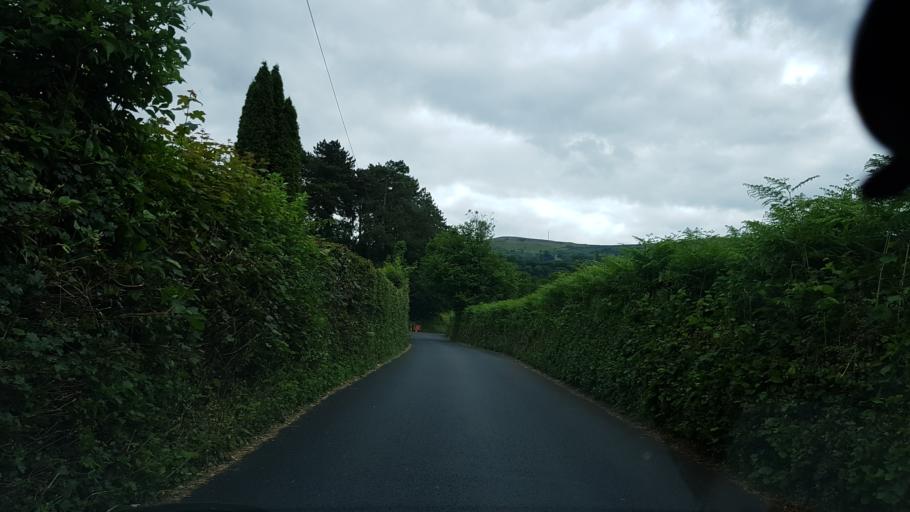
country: GB
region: Wales
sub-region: Monmouthshire
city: Gilwern
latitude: 51.8313
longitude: -3.0958
